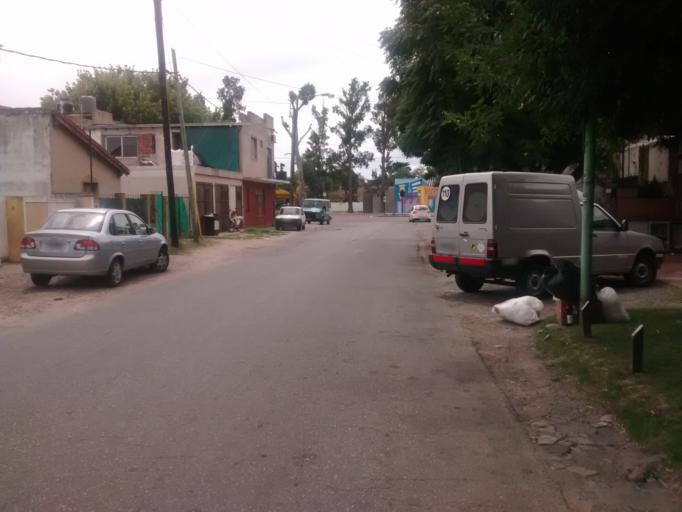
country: AR
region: Buenos Aires
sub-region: Partido de La Plata
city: La Plata
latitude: -34.8634
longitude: -58.0539
